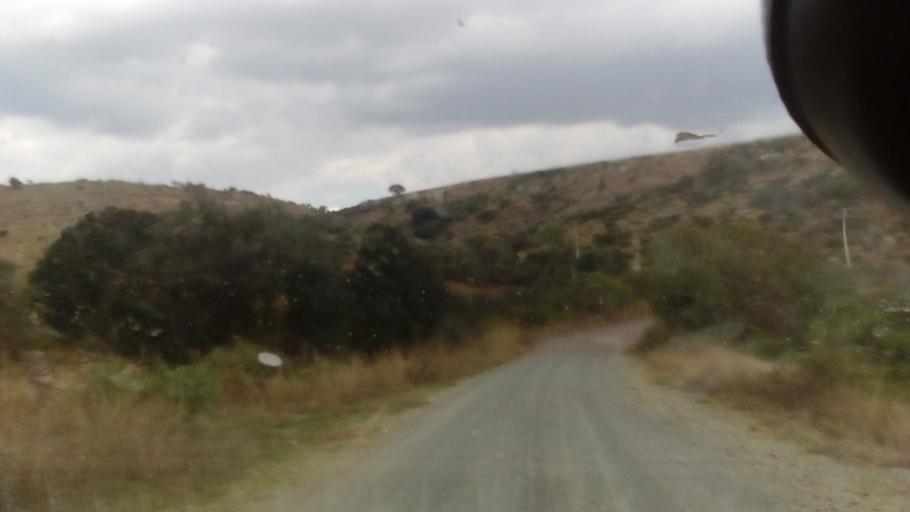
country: MX
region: Guanajuato
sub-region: Silao de la Victoria
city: San Francisco (Banos de Agua Caliente)
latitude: 21.1969
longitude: -101.4555
